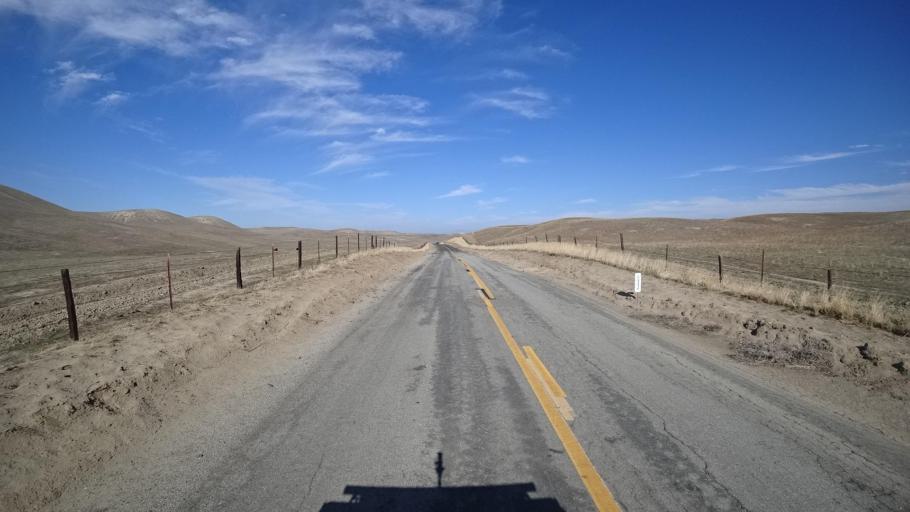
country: US
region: California
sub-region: Tulare County
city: Richgrove
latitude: 35.6404
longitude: -118.9430
